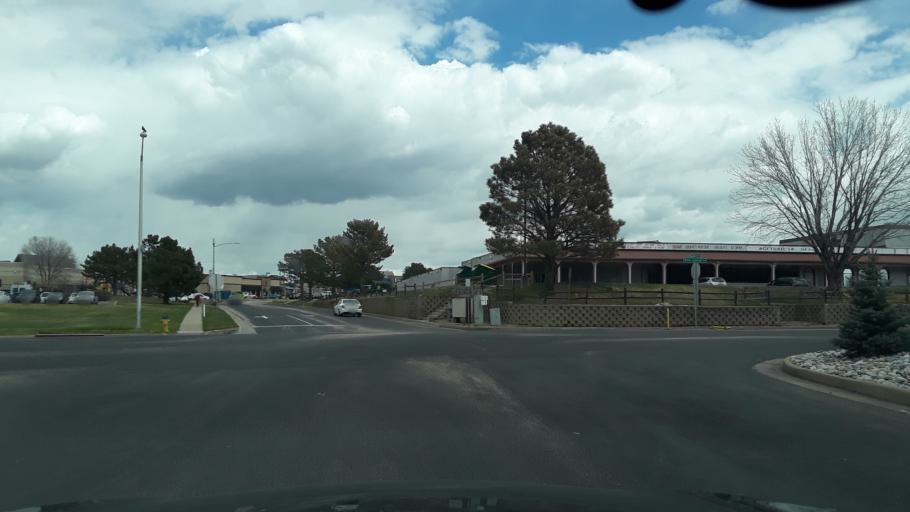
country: US
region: Colorado
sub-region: El Paso County
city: Air Force Academy
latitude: 38.9452
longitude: -104.8038
